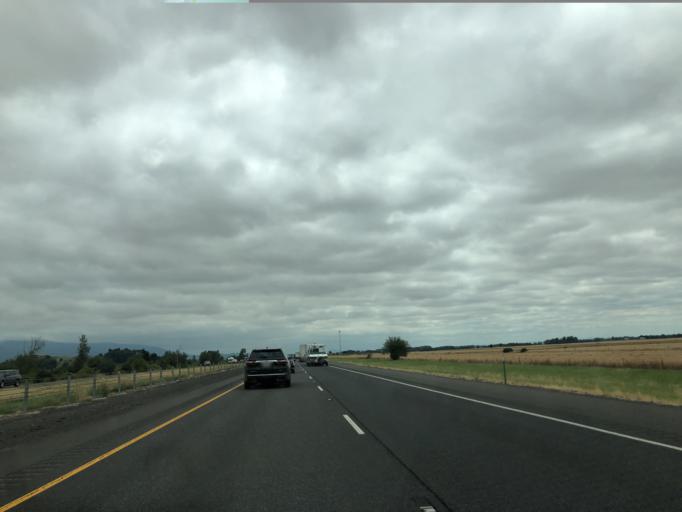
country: US
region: Oregon
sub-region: Linn County
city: Brownsville
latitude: 44.3357
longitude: -123.0613
